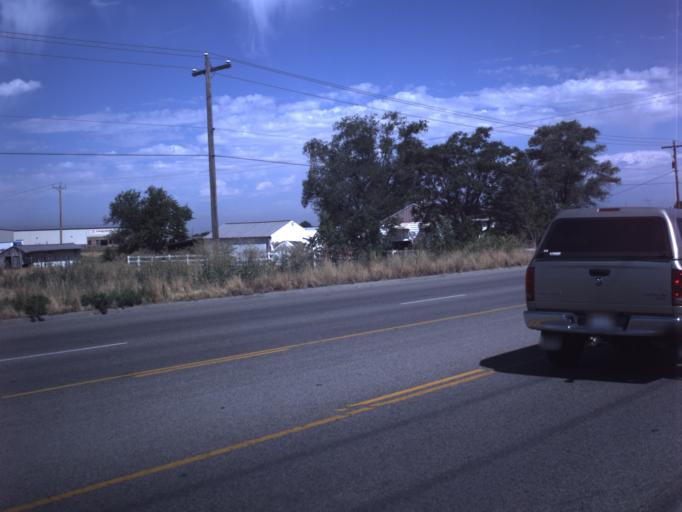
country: US
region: Utah
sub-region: Weber County
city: West Haven
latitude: 41.2113
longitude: -112.0257
